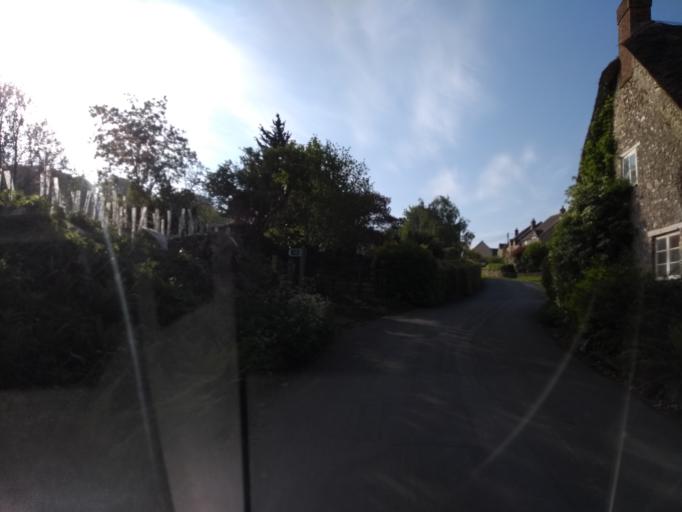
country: GB
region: England
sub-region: Devon
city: Axminster
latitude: 50.8009
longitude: -2.9358
